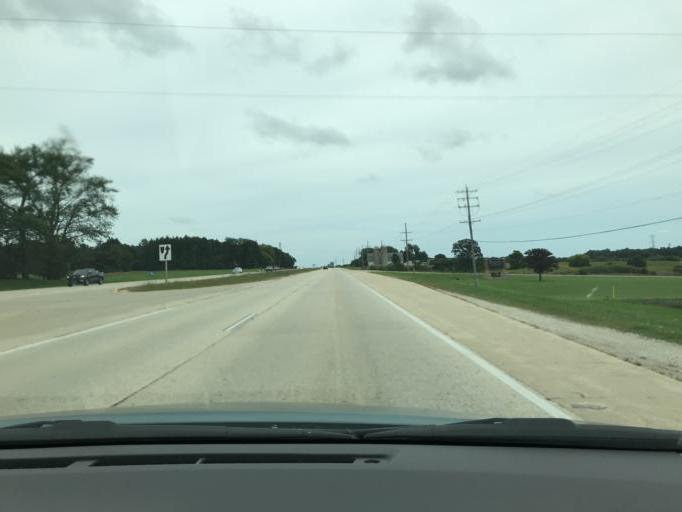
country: US
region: Wisconsin
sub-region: Kenosha County
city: Pleasant Prairie
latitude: 42.5672
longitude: -87.9779
